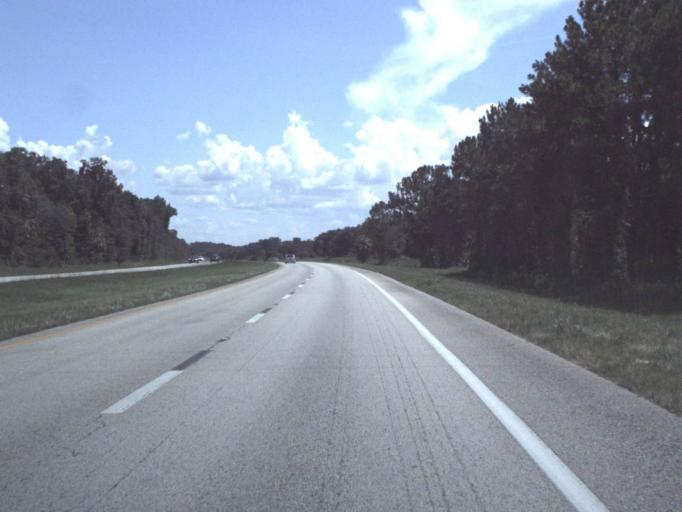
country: US
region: Florida
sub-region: Alachua County
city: Hawthorne
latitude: 29.5242
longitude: -82.1029
